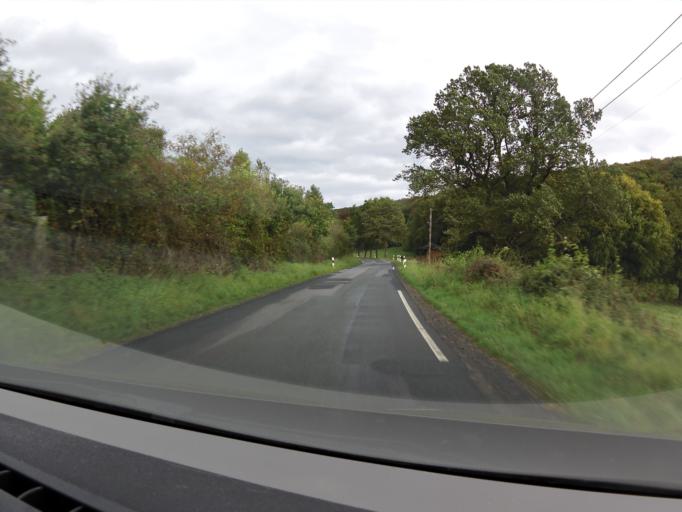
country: DE
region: Lower Saxony
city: Derental
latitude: 51.6970
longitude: 9.4409
